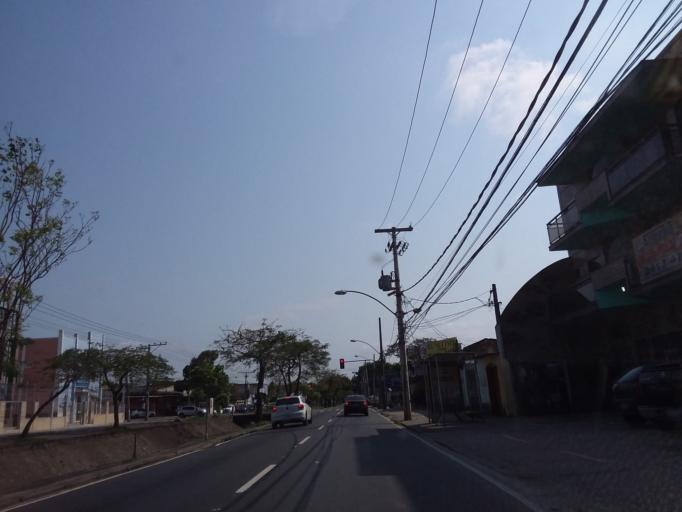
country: BR
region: Rio de Janeiro
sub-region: Nilopolis
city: Nilopolis
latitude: -22.8986
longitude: -43.5413
